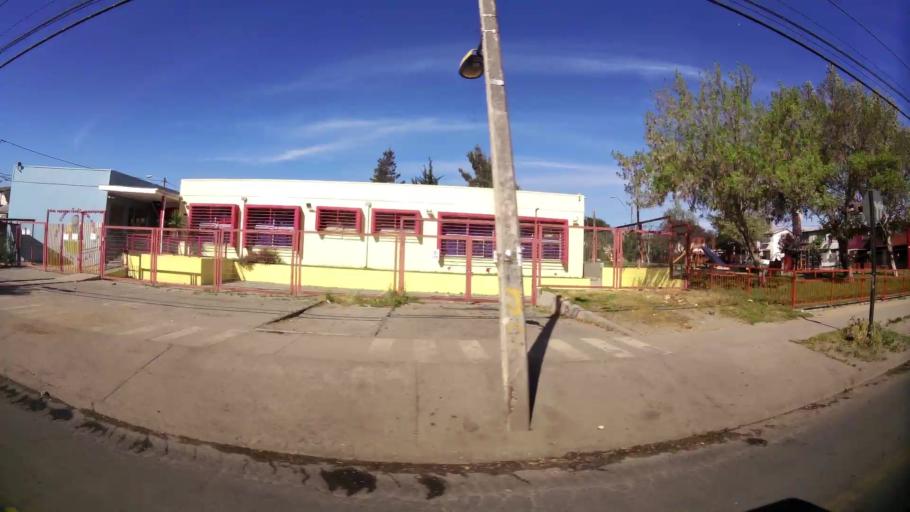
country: CL
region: Santiago Metropolitan
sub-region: Provincia de Santiago
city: Lo Prado
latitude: -33.4941
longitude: -70.7360
